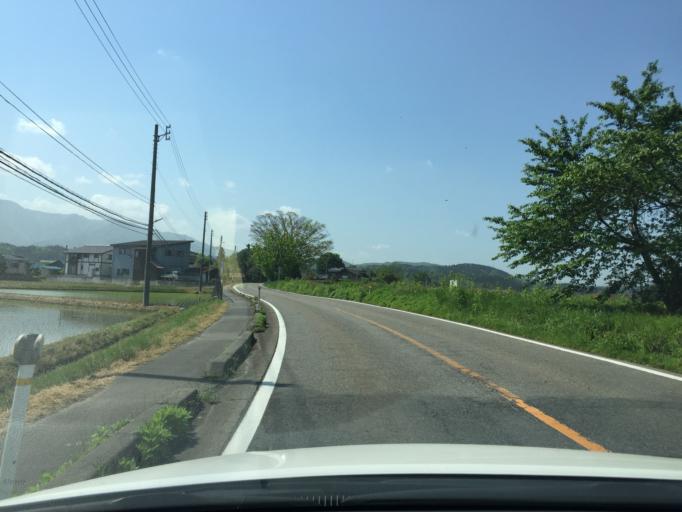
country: JP
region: Niigata
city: Muramatsu
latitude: 37.6801
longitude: 139.1496
